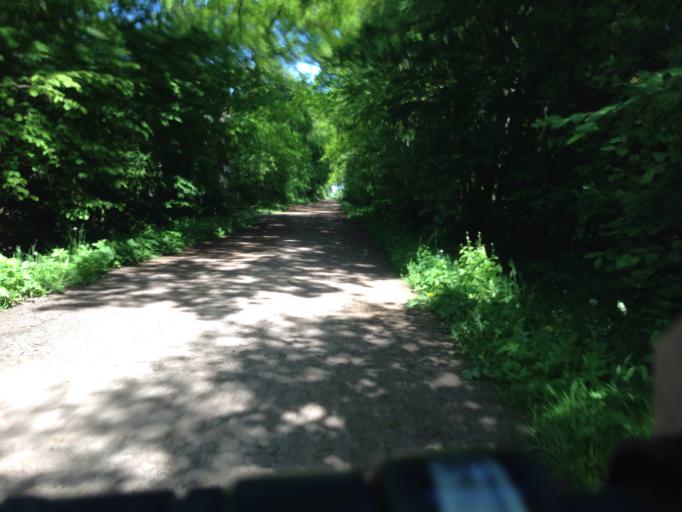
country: DE
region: Schleswig-Holstein
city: Stapelfeld
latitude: 53.5893
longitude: 10.1912
